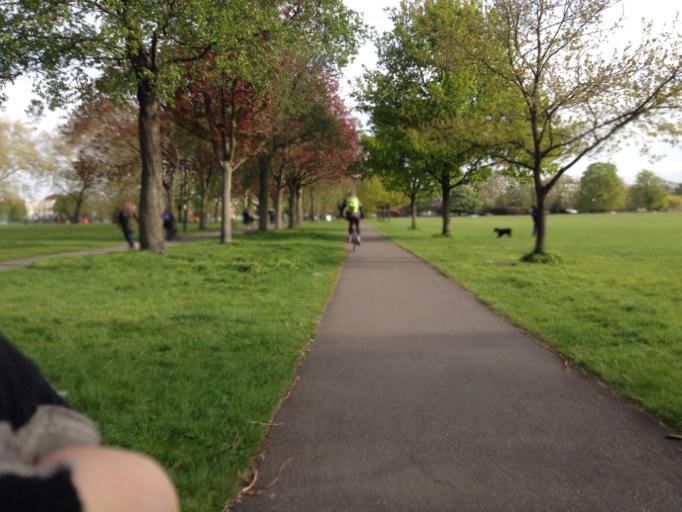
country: GB
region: England
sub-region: Greater London
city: Battersea
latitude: 51.4585
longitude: -0.1481
